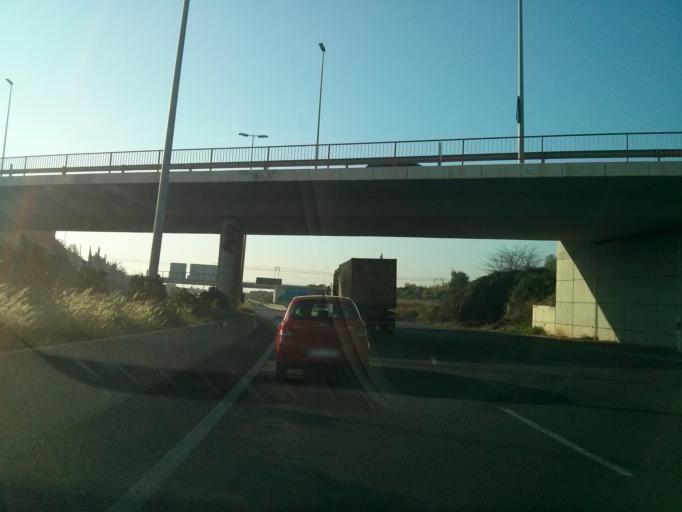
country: ES
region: Valencia
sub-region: Provincia de Valencia
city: Paterna
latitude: 39.4984
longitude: -0.4295
